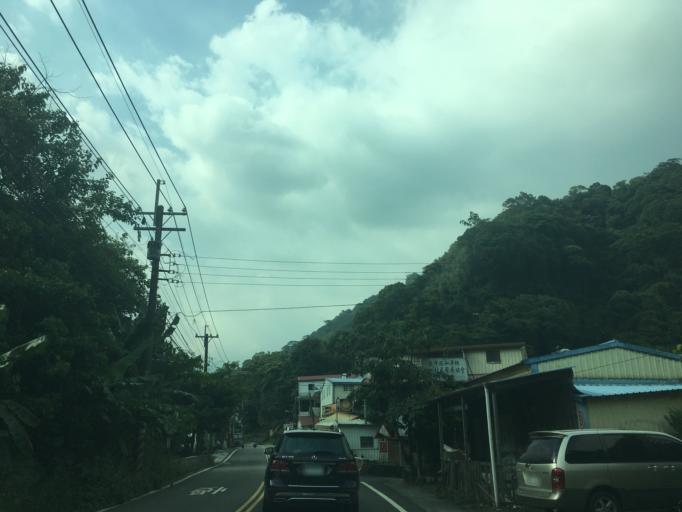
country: TW
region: Taiwan
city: Fengyuan
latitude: 24.3053
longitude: 120.9244
